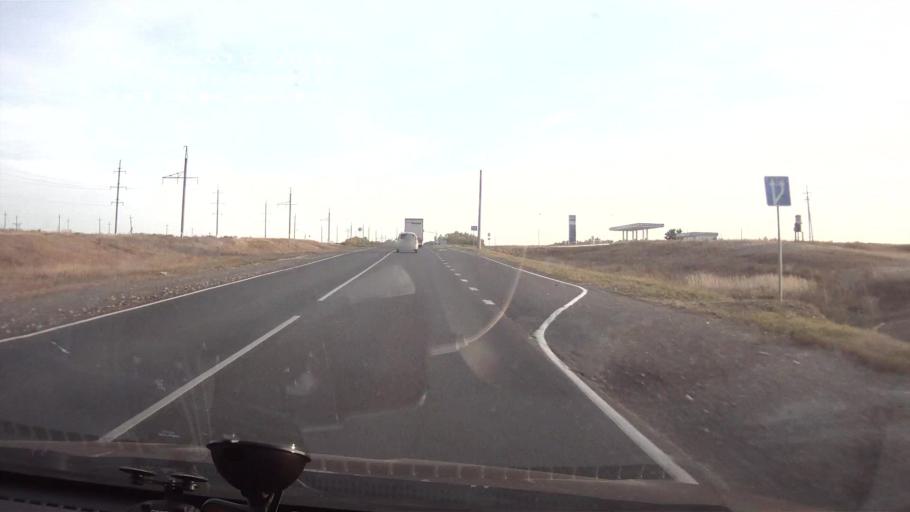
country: RU
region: Saratov
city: Krasnoarmeysk
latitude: 51.1695
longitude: 45.6489
